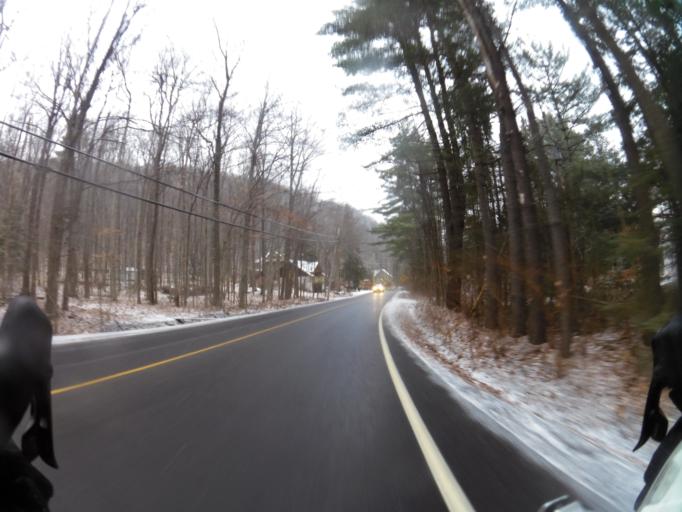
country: CA
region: Quebec
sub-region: Outaouais
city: Gatineau
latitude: 45.4969
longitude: -75.8271
